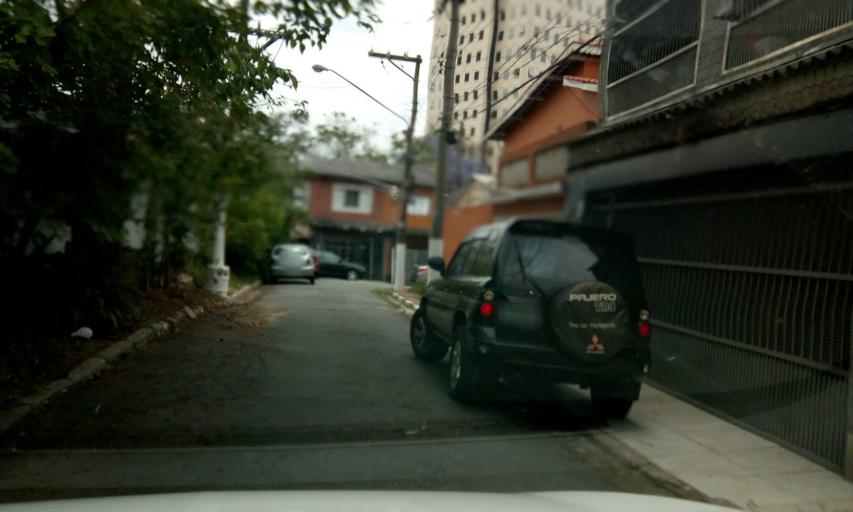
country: BR
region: Sao Paulo
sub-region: Sao Paulo
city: Sao Paulo
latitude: -23.5141
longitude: -46.7061
